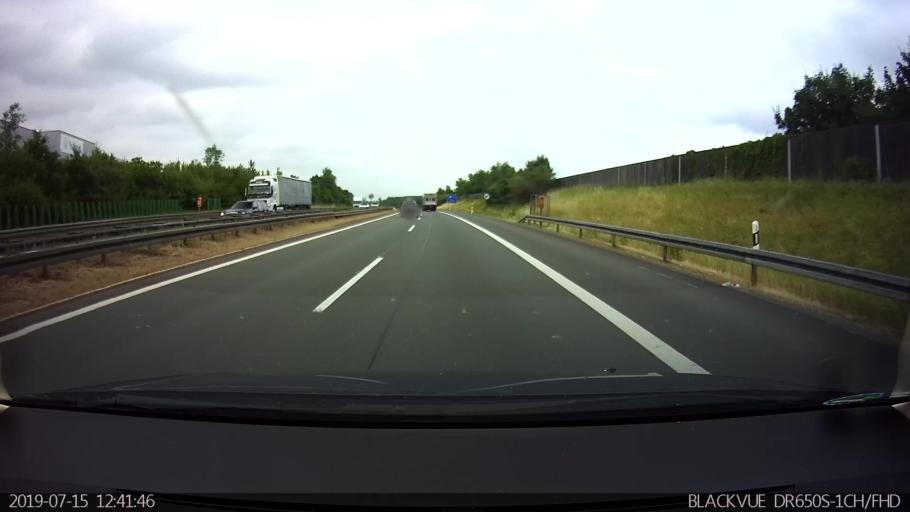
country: DE
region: Saxony
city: Treuen
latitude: 50.5413
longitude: 12.2604
